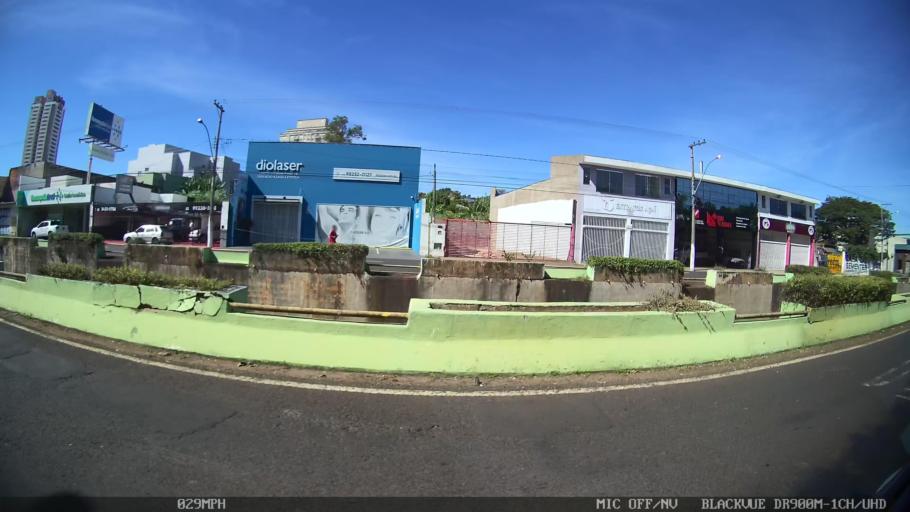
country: BR
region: Sao Paulo
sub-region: Franca
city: Franca
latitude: -20.5427
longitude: -47.3965
